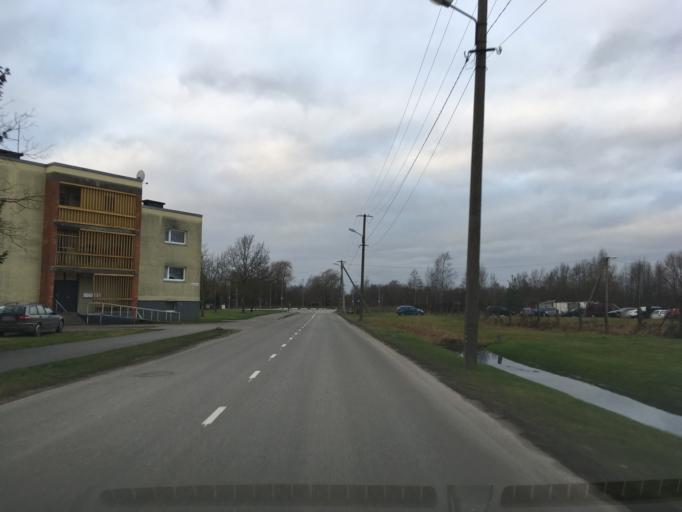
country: EE
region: Paernumaa
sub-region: Paernu linn
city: Parnu
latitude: 58.3988
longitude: 24.4857
